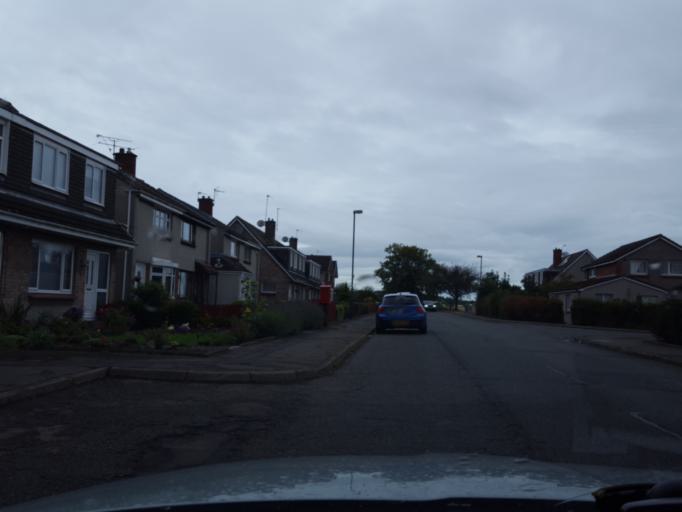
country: GB
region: Scotland
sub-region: Midlothian
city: Bonnyrigg
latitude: 55.8717
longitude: -3.1258
